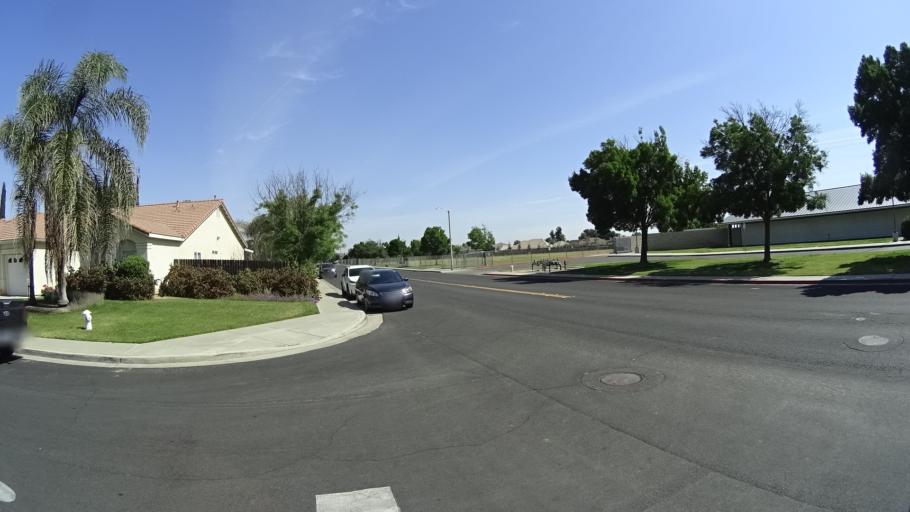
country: US
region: California
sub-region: Kings County
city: Hanford
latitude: 36.3461
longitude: -119.6686
